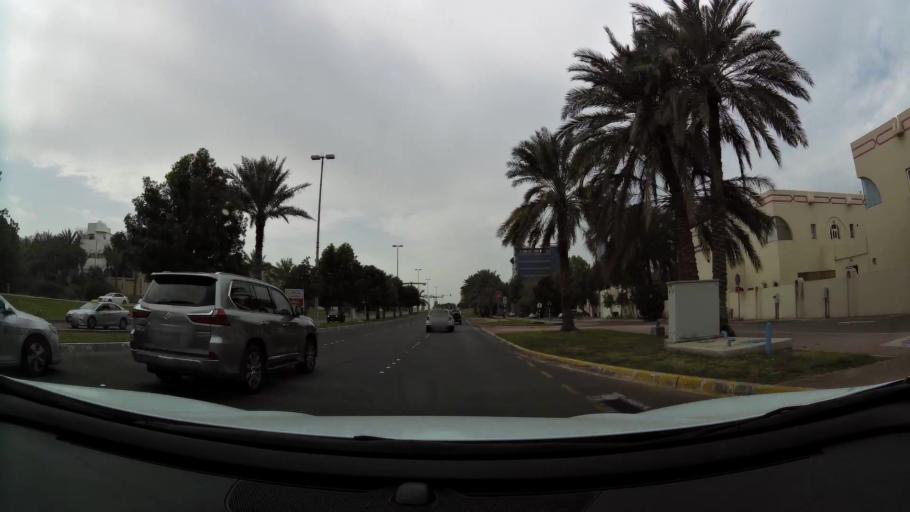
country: AE
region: Abu Dhabi
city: Abu Dhabi
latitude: 24.4652
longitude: 54.3377
